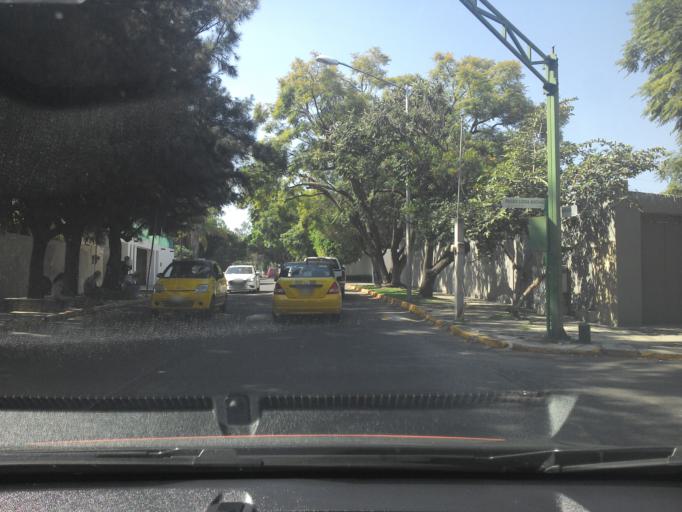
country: MX
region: Jalisco
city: Zapopan2
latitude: 20.6941
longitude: -103.4030
